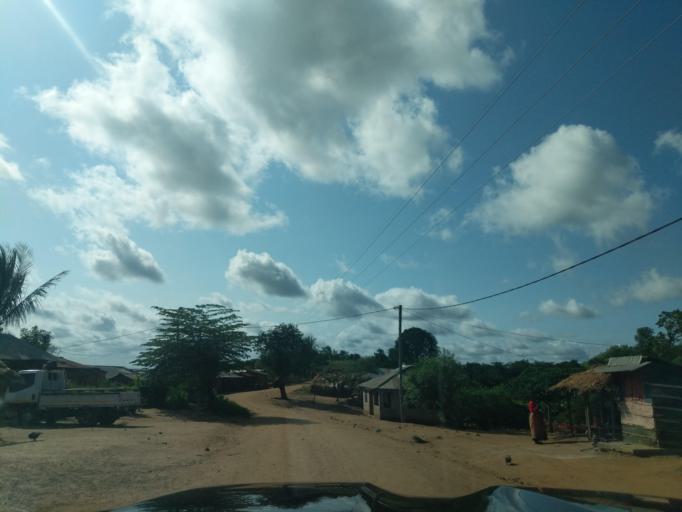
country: TZ
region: Tanga
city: Muheza
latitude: -5.4223
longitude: 38.6351
